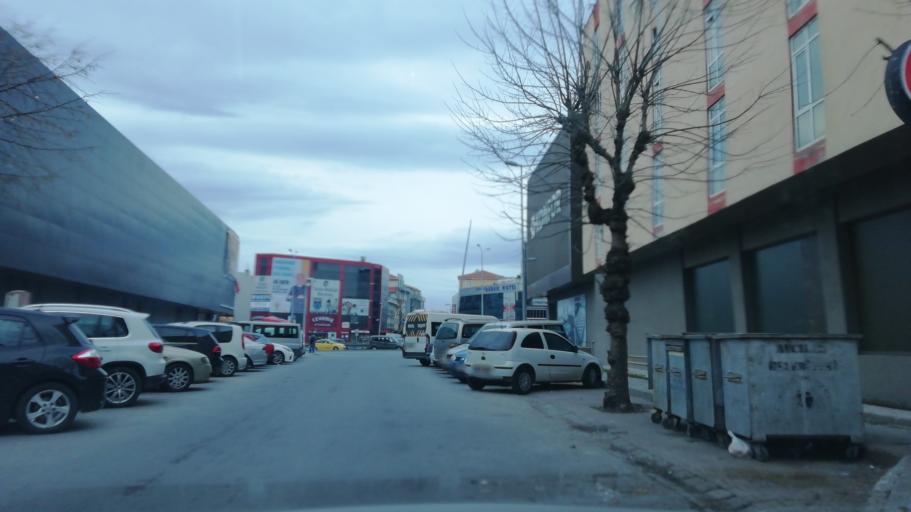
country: TR
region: Istanbul
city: Yakuplu
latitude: 40.9943
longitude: 28.7091
